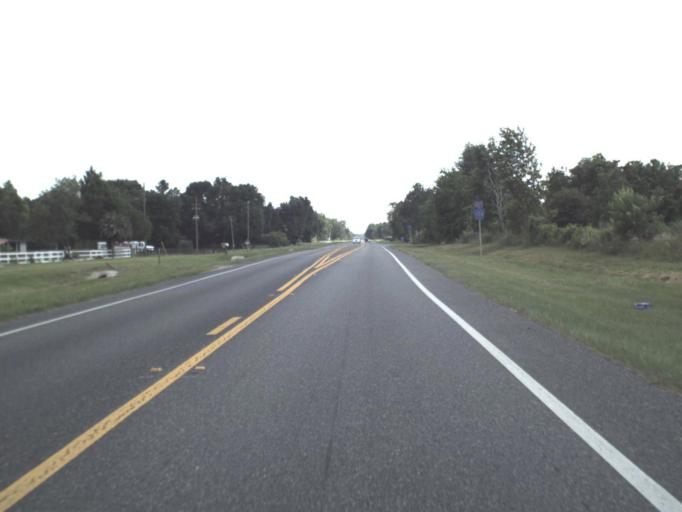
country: US
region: Florida
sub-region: Alachua County
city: High Springs
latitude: 29.8893
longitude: -82.6092
